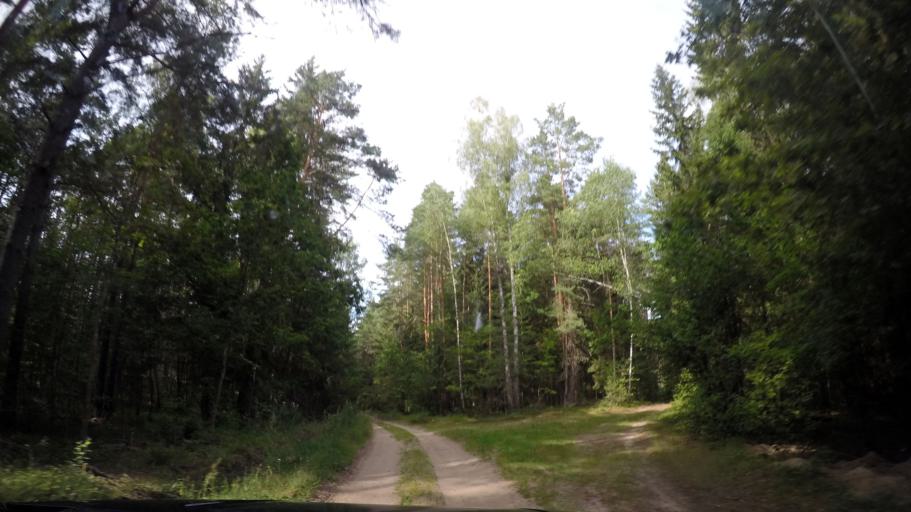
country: BY
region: Grodnenskaya
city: Skidal'
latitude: 53.8268
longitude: 24.1794
